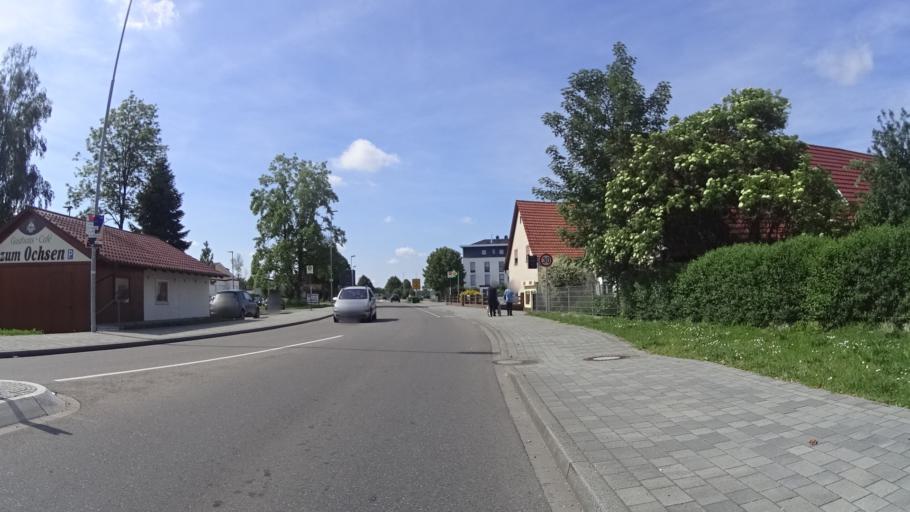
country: DE
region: Baden-Wuerttemberg
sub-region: Freiburg Region
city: Kehl
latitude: 48.5199
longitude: 7.8215
